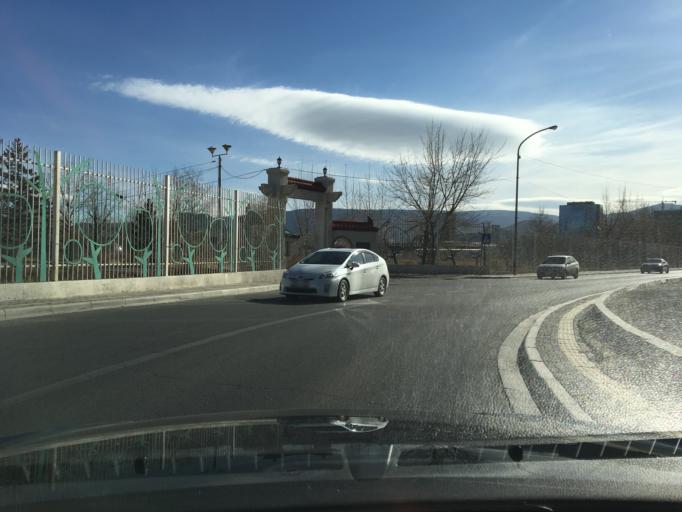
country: MN
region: Ulaanbaatar
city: Ulaanbaatar
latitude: 47.9104
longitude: 106.9150
